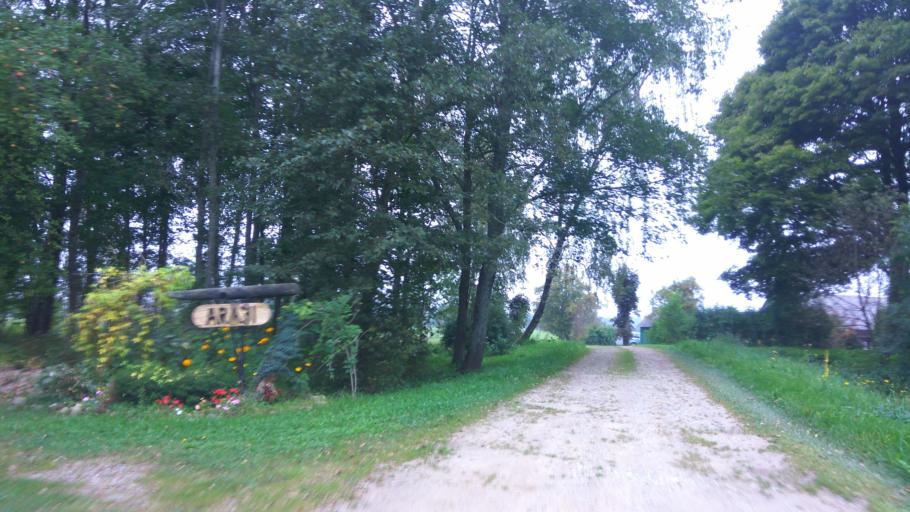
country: LV
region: Rucavas
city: Rucava
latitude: 56.1665
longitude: 21.1753
